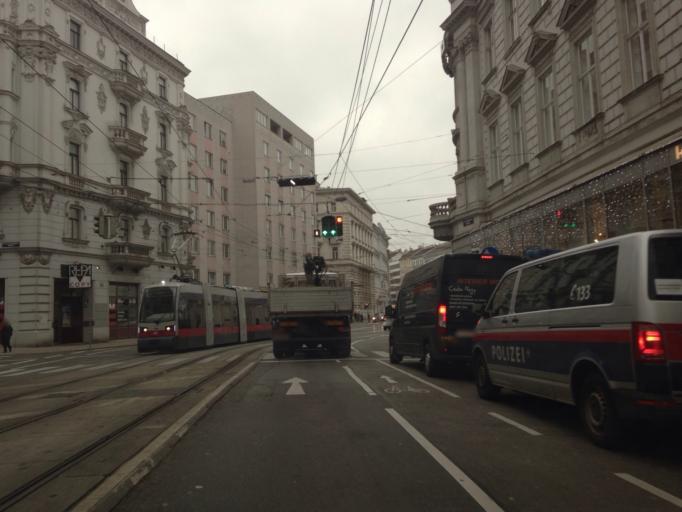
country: AT
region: Vienna
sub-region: Wien Stadt
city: Vienna
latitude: 48.2242
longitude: 16.3540
